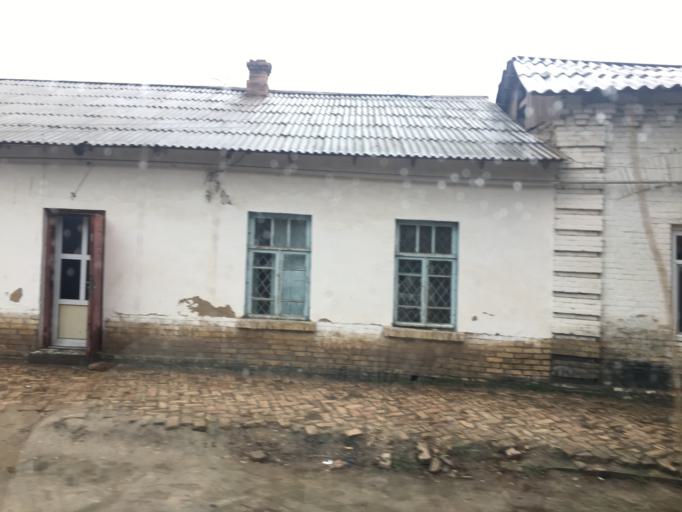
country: TM
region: Mary
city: Yoloeten
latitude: 37.2990
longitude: 62.3614
